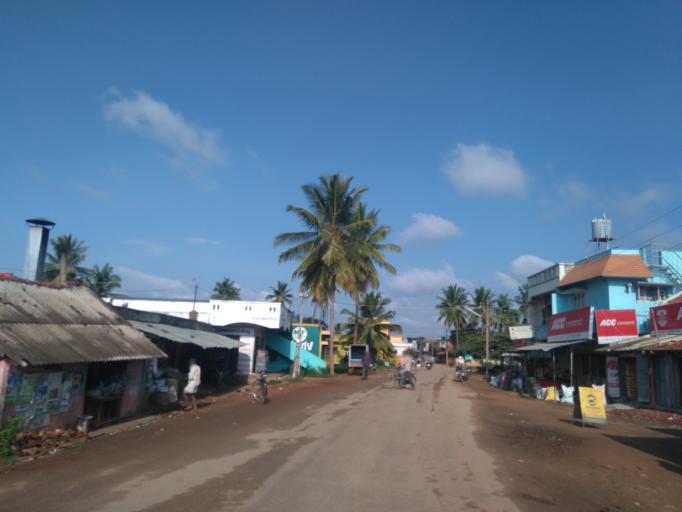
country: IN
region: Karnataka
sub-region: Mysore
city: Tirumakudal Narsipur
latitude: 12.2577
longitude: 77.0120
